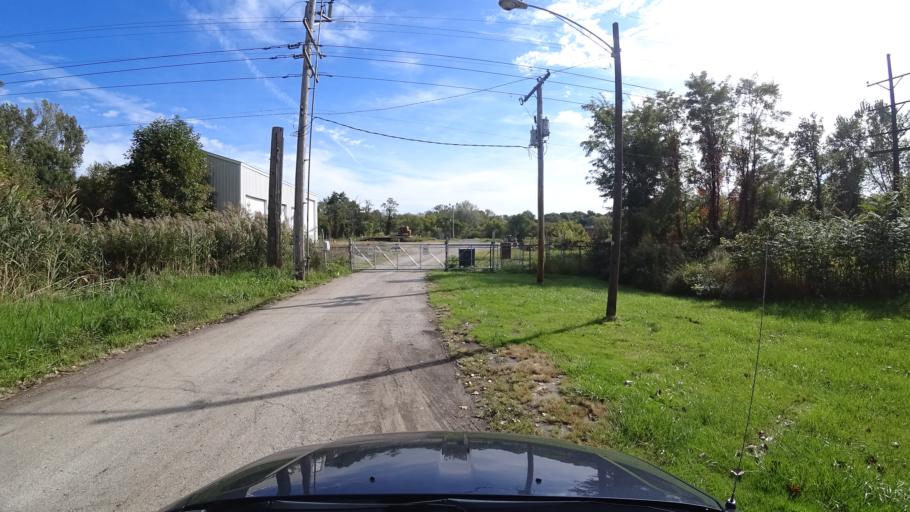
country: US
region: Indiana
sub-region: LaPorte County
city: Michigan City
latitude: 41.7197
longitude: -86.8849
